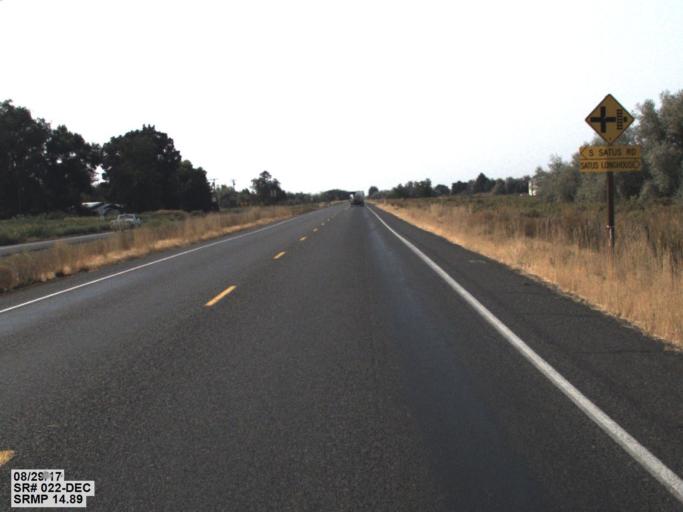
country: US
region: Washington
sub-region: Yakima County
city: Granger
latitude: 46.2687
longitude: -120.1476
